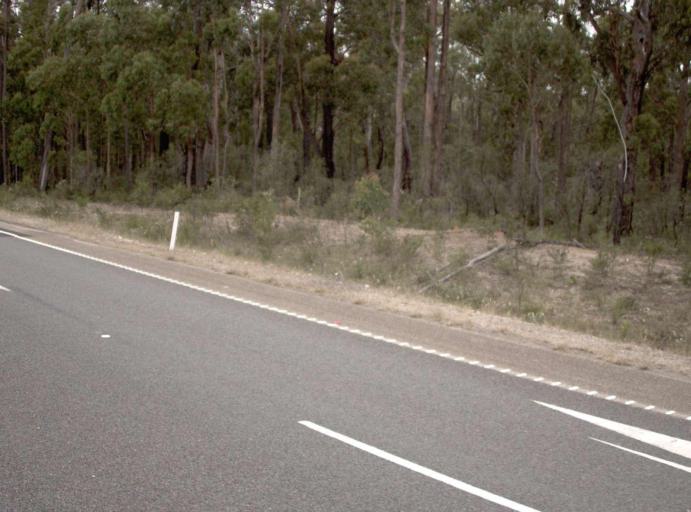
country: AU
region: Victoria
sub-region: East Gippsland
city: Lakes Entrance
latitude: -37.7009
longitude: 147.9935
